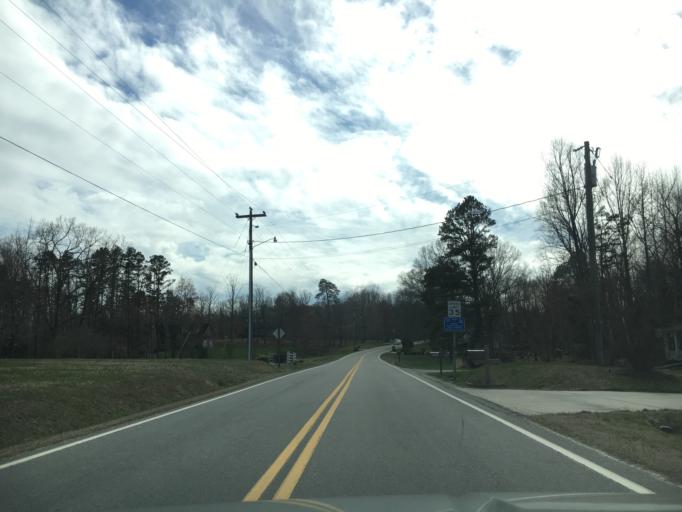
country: US
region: Virginia
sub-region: Halifax County
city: Halifax
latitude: 36.7600
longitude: -78.9104
